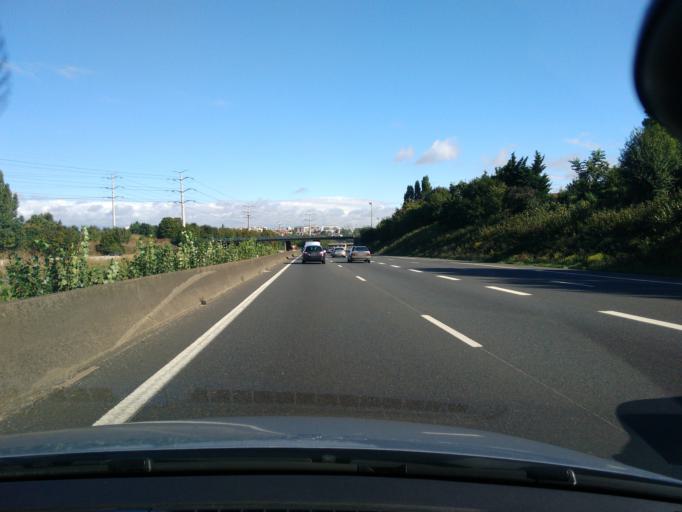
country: FR
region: Ile-de-France
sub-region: Departement de l'Essonne
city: Wissous
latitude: 48.7391
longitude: 2.3197
